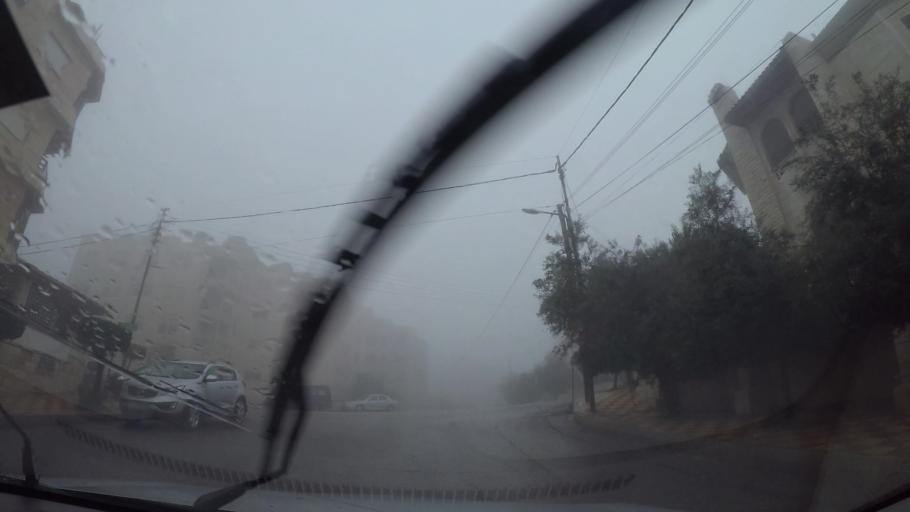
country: JO
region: Amman
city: Al Jubayhah
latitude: 32.0068
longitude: 35.8884
